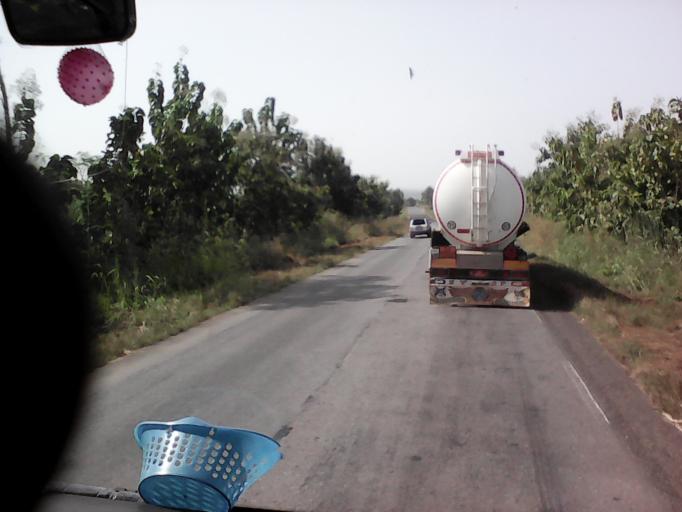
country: TG
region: Centrale
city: Sotouboua
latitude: 8.7632
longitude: 1.0596
